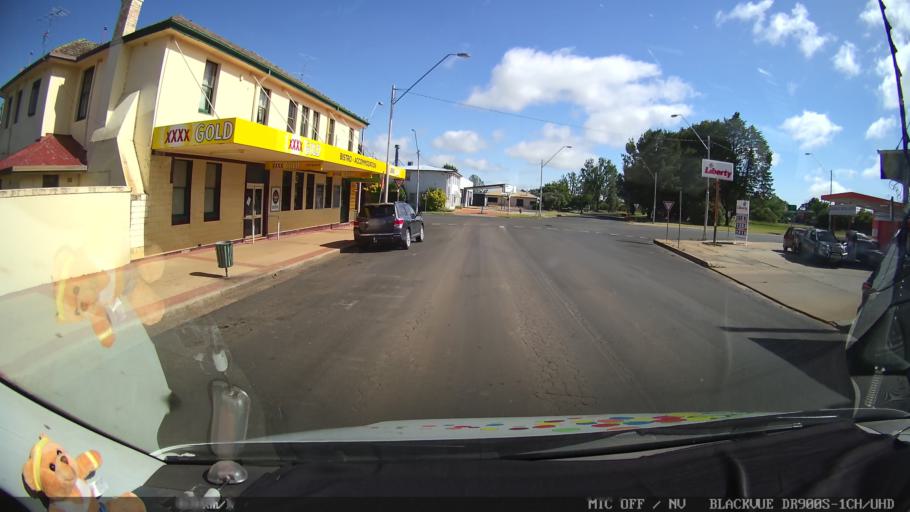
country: AU
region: New South Wales
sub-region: Guyra
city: Guyra
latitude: -30.2174
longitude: 151.6719
